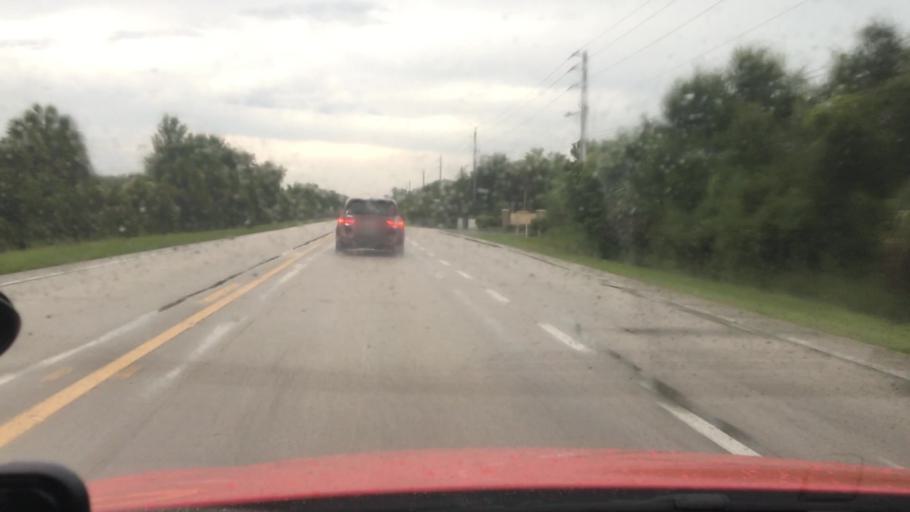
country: US
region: Florida
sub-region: Volusia County
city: Samsula-Spruce Creek
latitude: 29.0656
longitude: -81.0679
